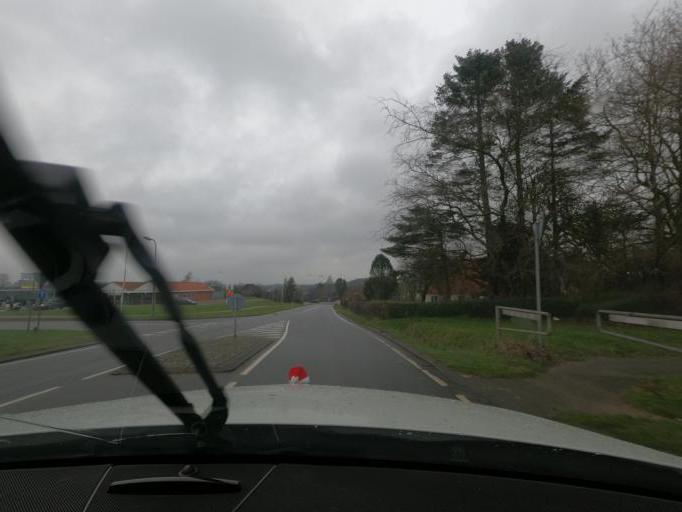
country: DK
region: South Denmark
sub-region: Haderslev Kommune
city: Starup
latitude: 55.2427
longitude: 9.5377
